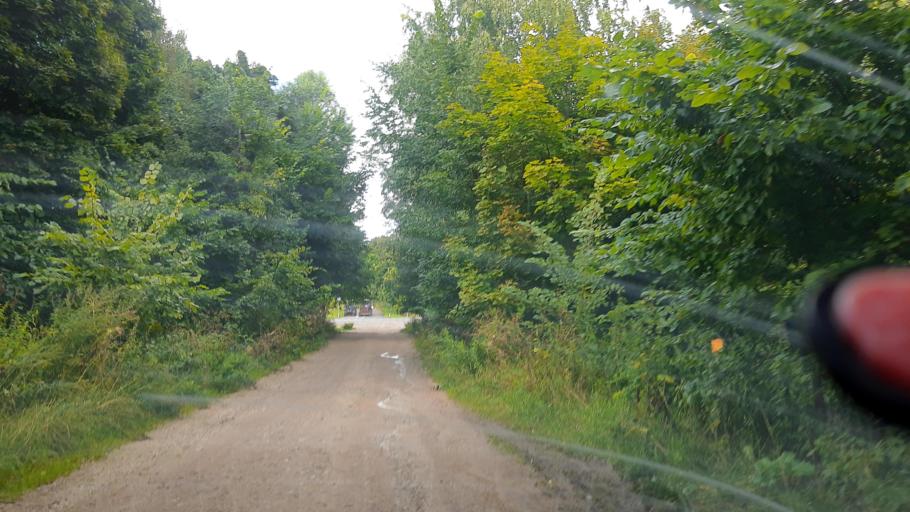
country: RU
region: Bashkortostan
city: Iglino
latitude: 54.7696
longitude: 56.4536
